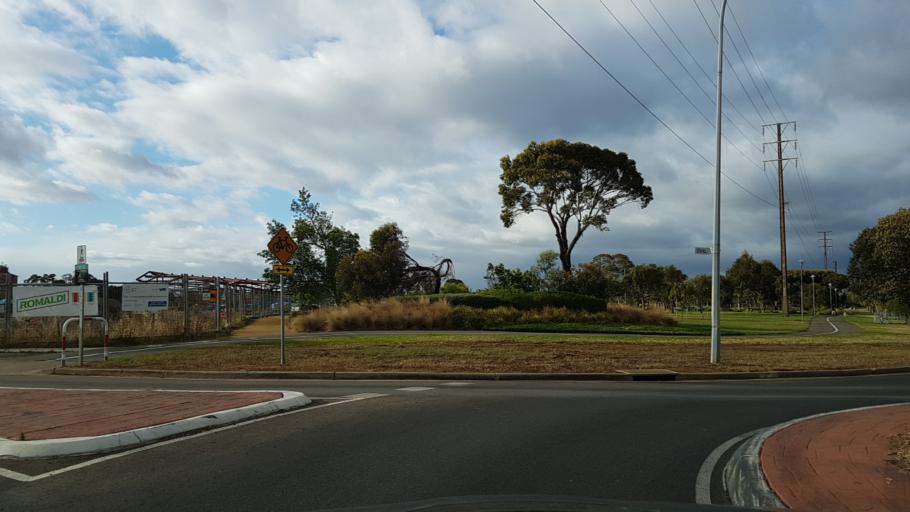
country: AU
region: South Australia
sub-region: City of West Torrens
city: Plympton
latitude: -34.9543
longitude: 138.5589
